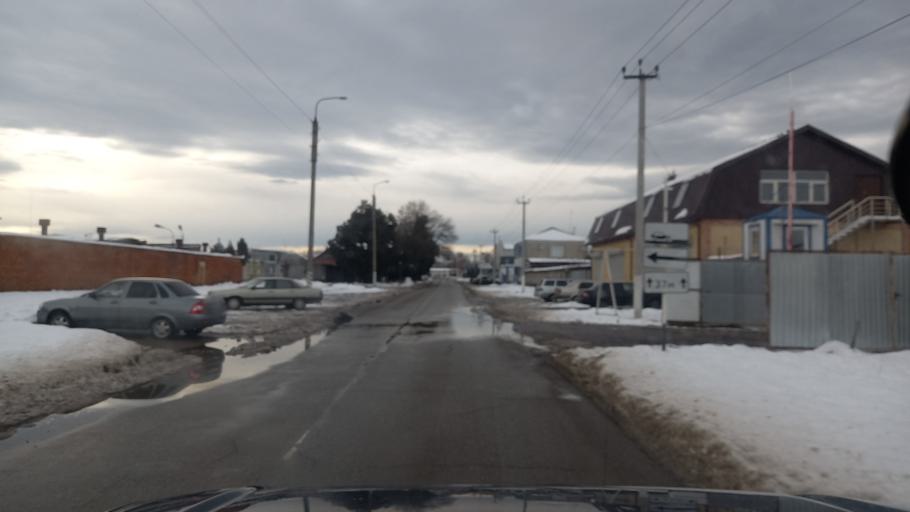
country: RU
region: Adygeya
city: Maykop
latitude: 44.6251
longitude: 40.0584
